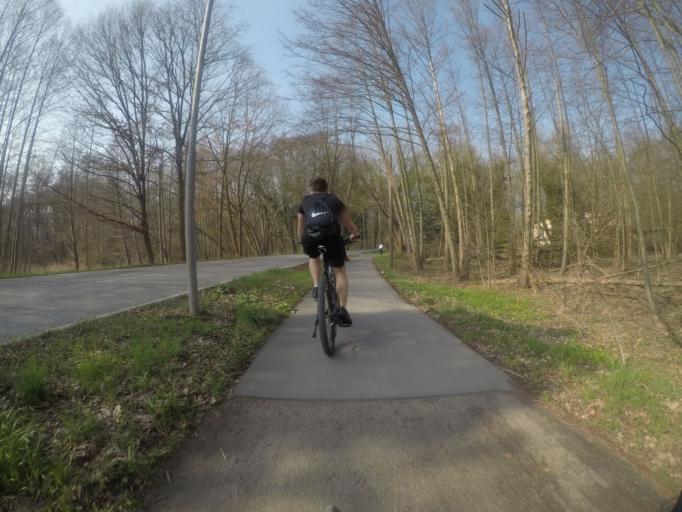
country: DE
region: Brandenburg
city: Konigs Wusterhausen
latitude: 52.2864
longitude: 13.6525
